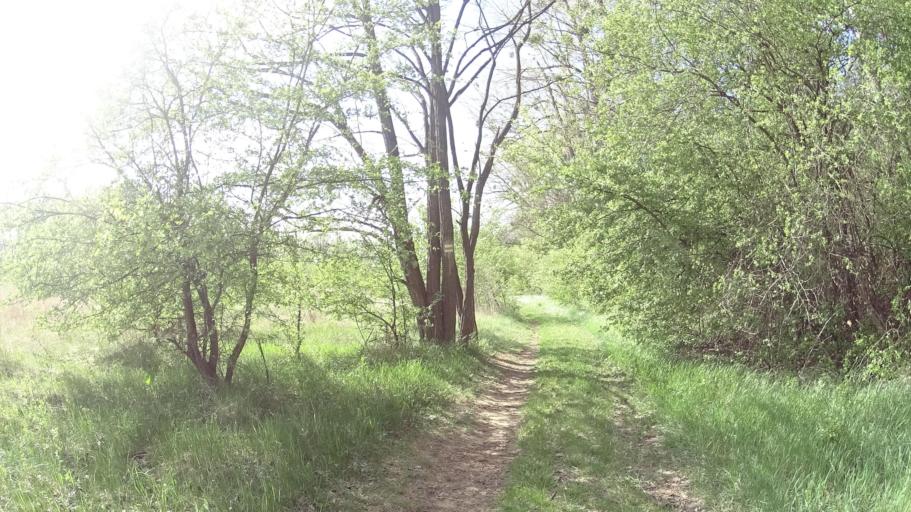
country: HU
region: Pest
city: Veresegyhaz
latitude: 47.6261
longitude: 19.2906
